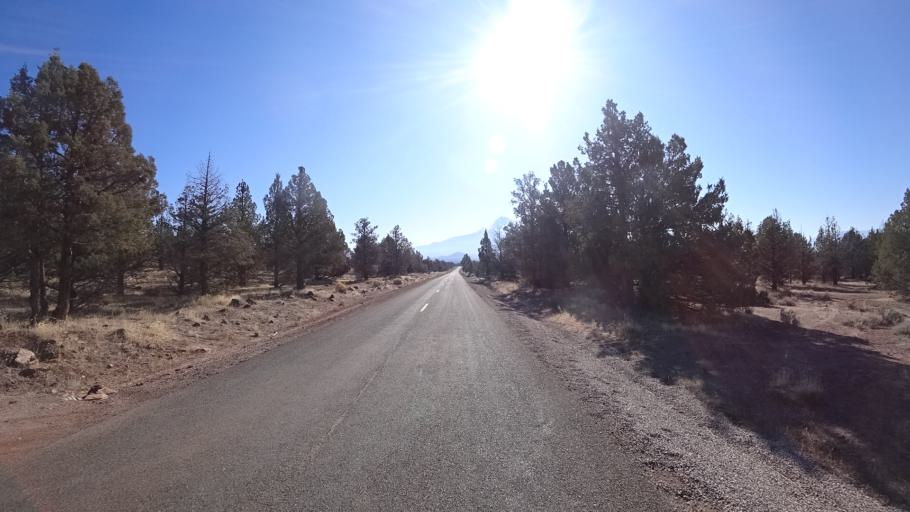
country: US
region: California
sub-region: Siskiyou County
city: Weed
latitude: 41.6098
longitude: -122.3114
